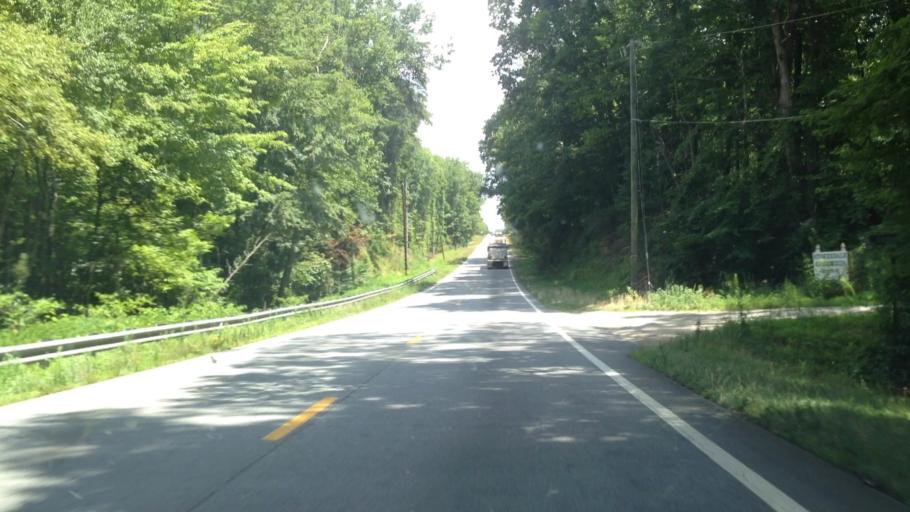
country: US
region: North Carolina
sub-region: Guilford County
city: Stokesdale
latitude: 36.2637
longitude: -79.9533
